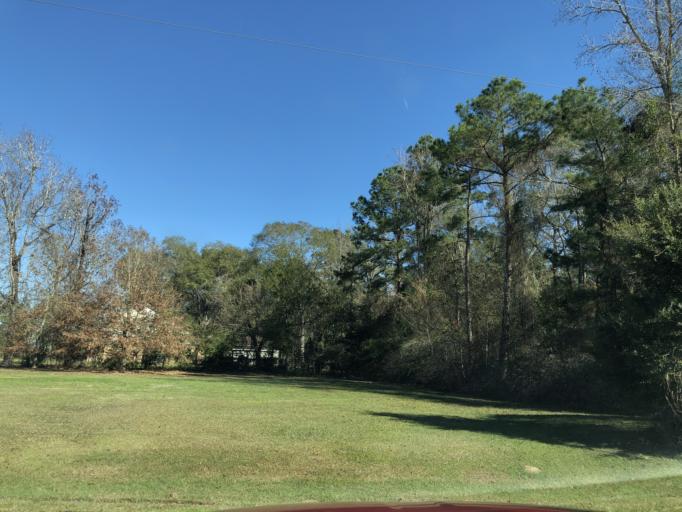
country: US
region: Texas
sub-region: Montgomery County
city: Splendora
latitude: 30.2292
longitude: -95.1642
